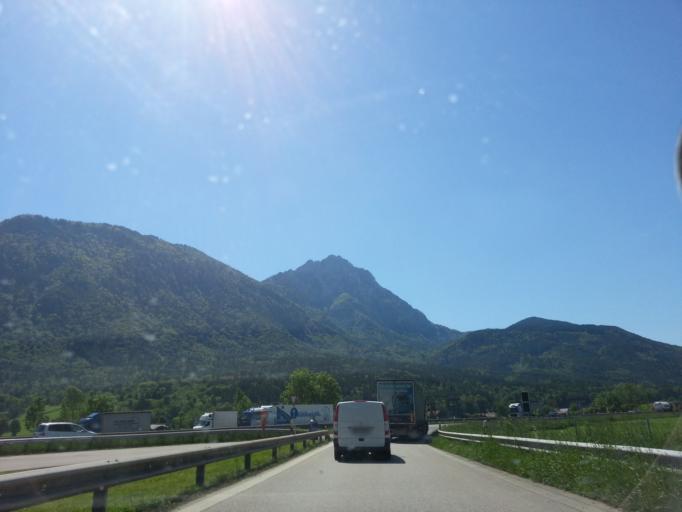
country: DE
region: Bavaria
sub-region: Upper Bavaria
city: Piding
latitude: 47.7677
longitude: 12.9028
